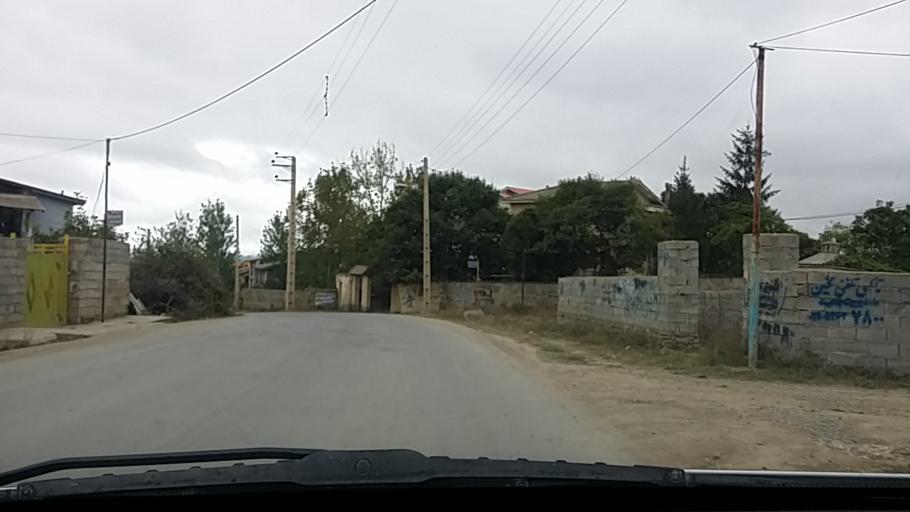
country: IR
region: Mazandaran
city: `Abbasabad
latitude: 36.4996
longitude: 51.1569
